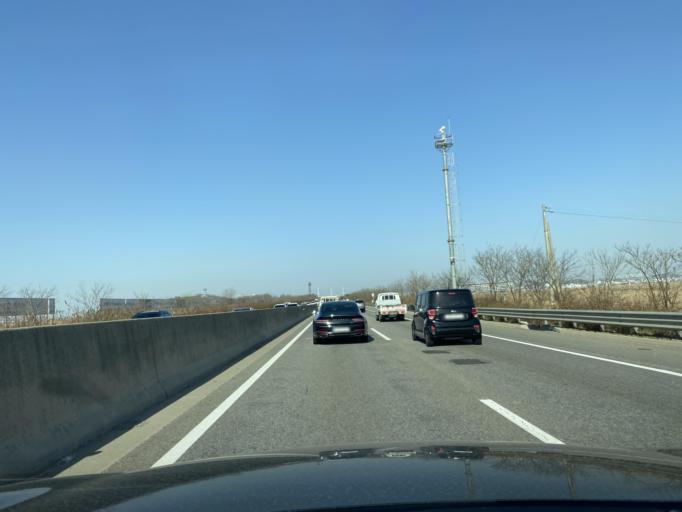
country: KR
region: Gyeonggi-do
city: Hwaseong-si
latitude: 37.2650
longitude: 126.7460
